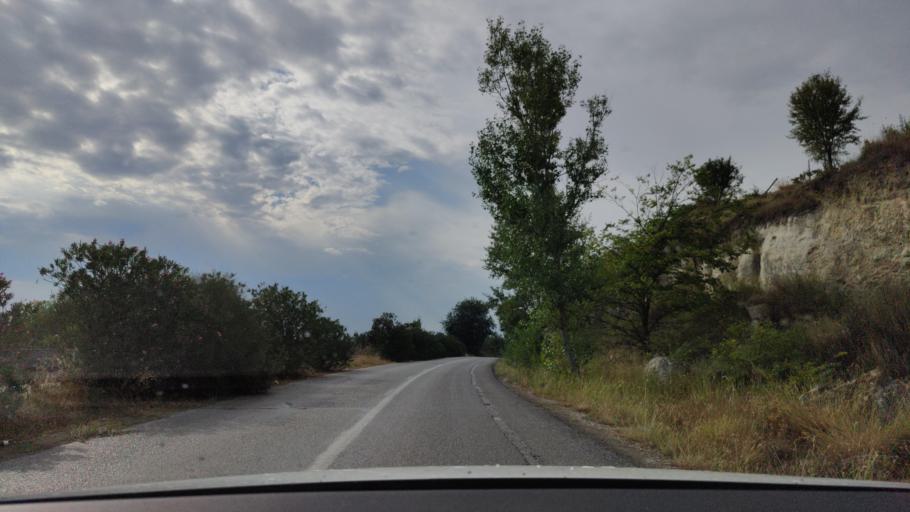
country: GR
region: Central Macedonia
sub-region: Nomos Serron
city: Lefkonas
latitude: 41.1056
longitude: 23.4756
